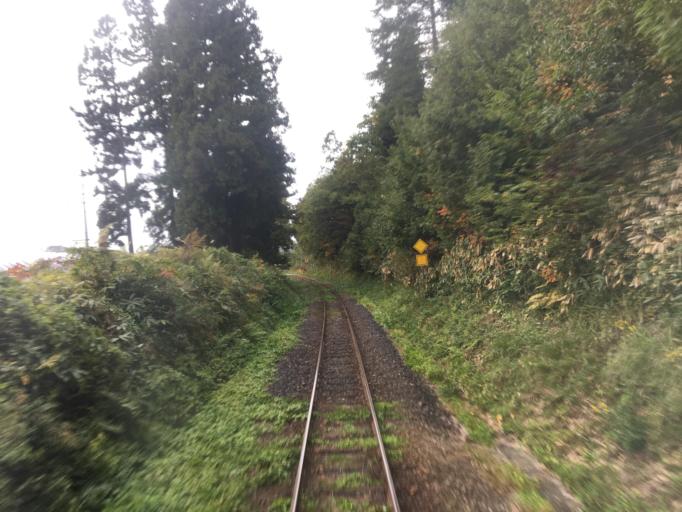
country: JP
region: Yamagata
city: Nagai
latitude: 38.0546
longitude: 140.0743
